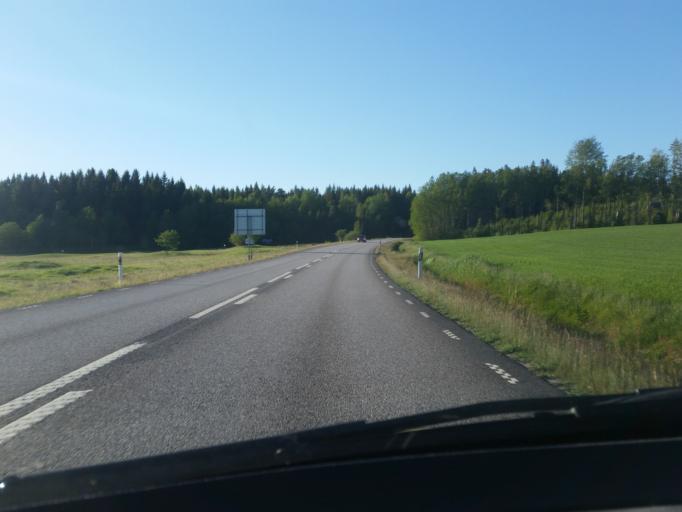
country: SE
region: Vaestra Goetaland
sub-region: Fargelanda Kommun
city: Faergelanda
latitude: 58.5228
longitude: 11.9786
